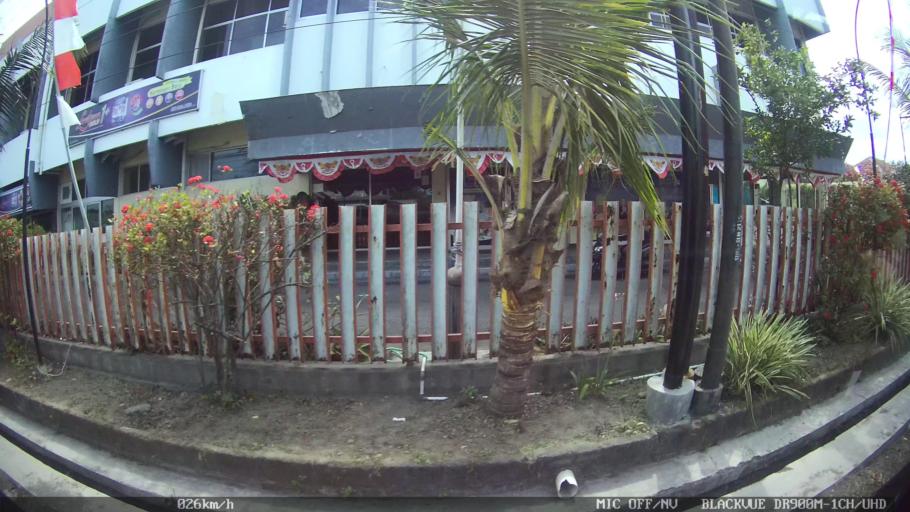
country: ID
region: Daerah Istimewa Yogyakarta
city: Depok
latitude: -7.7796
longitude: 110.4347
